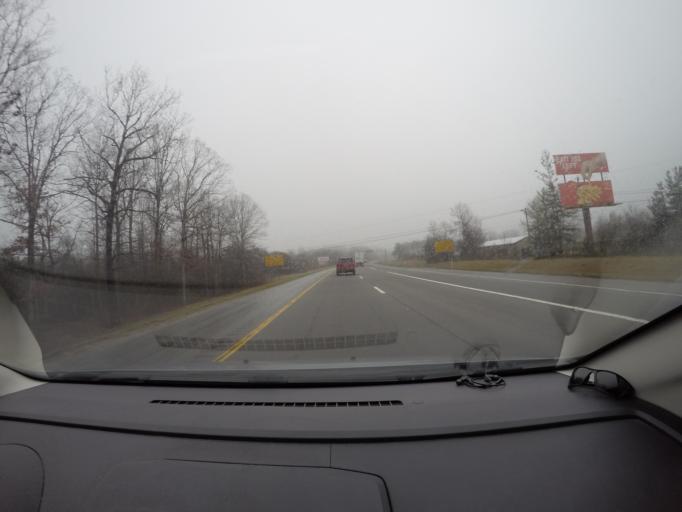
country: US
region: Tennessee
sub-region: Marion County
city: Monteagle
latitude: 35.2285
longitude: -85.8244
